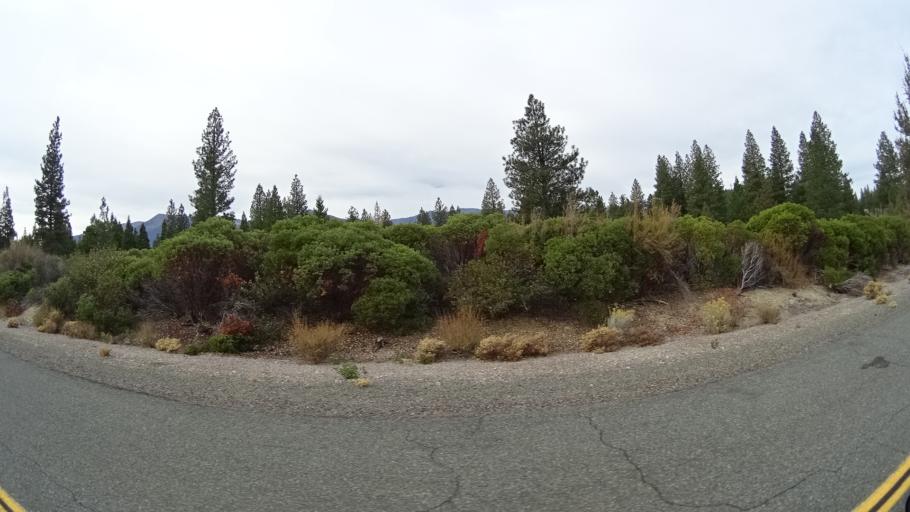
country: US
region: California
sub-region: Siskiyou County
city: Weed
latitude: 41.4119
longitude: -122.3648
